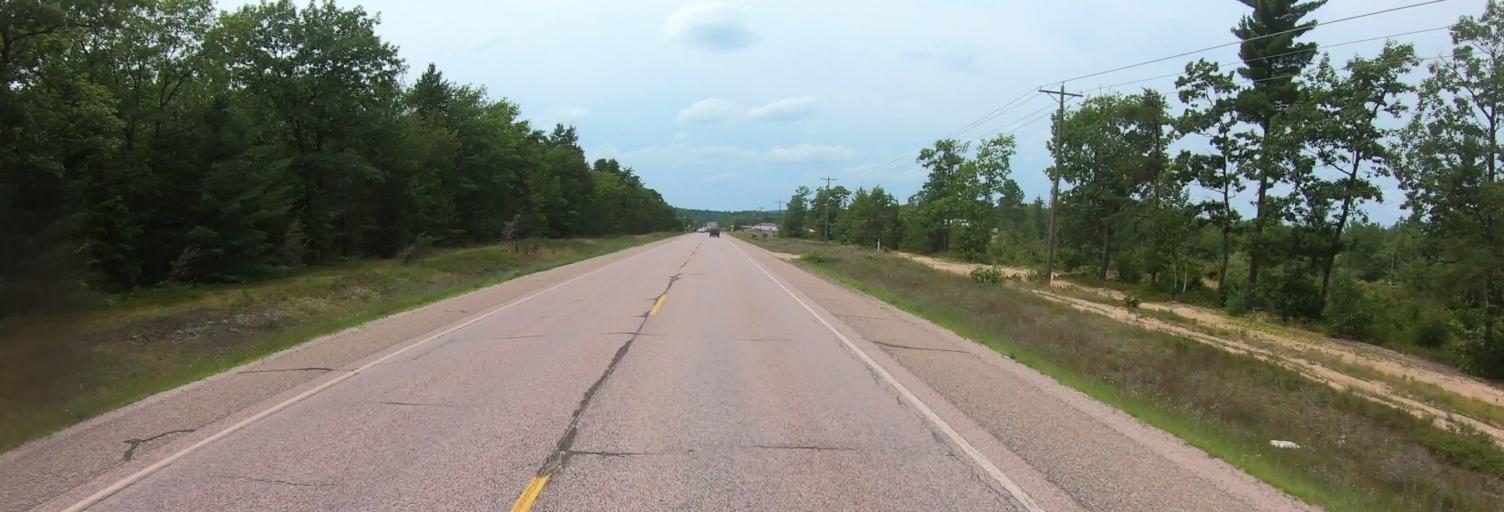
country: US
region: Michigan
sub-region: Marquette County
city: Harvey
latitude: 46.4616
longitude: -87.4188
